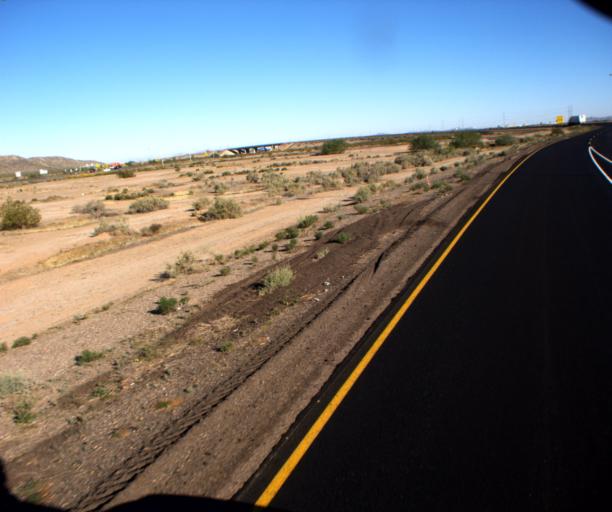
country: US
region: Arizona
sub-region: Pinal County
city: Arizona City
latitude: 32.8152
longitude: -111.6784
